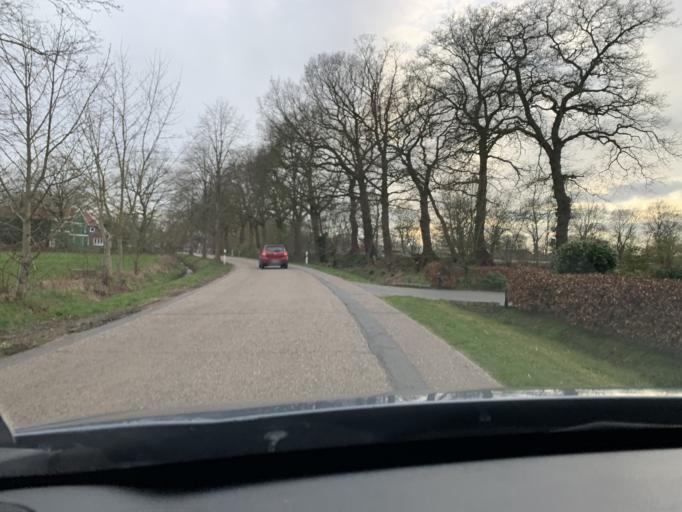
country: DE
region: Lower Saxony
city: Detern
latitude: 53.2562
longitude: 7.7178
